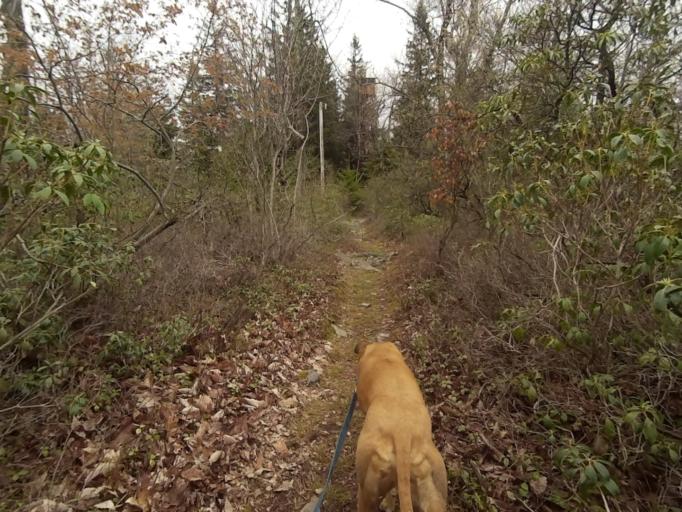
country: US
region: Pennsylvania
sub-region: Centre County
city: Boalsburg
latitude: 40.7514
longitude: -77.7550
